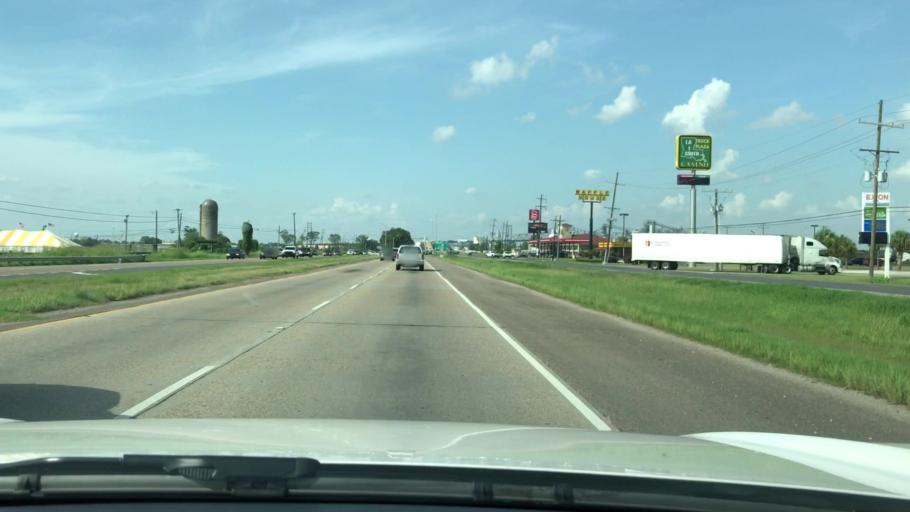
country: US
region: Louisiana
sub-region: West Baton Rouge Parish
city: Port Allen
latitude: 30.4224
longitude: -91.2185
